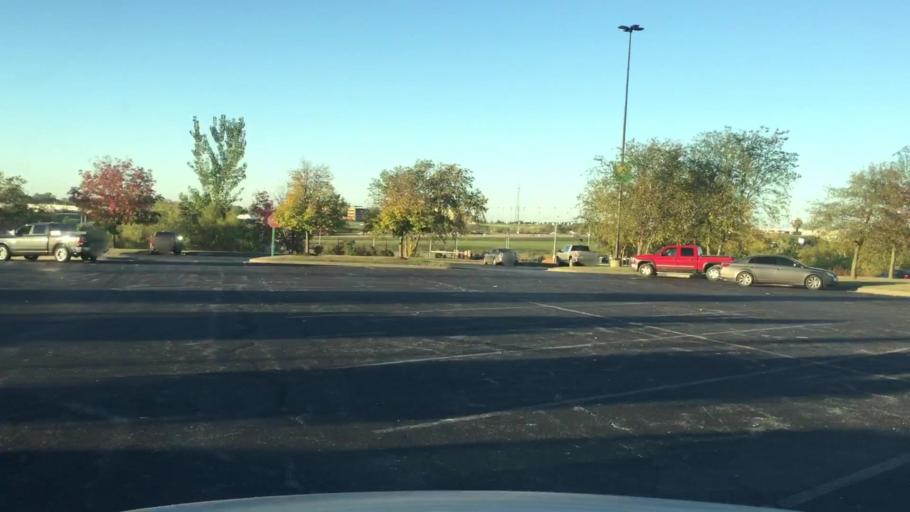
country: US
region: Kansas
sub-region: Wyandotte County
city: Edwardsville
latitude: 39.1198
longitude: -94.8168
